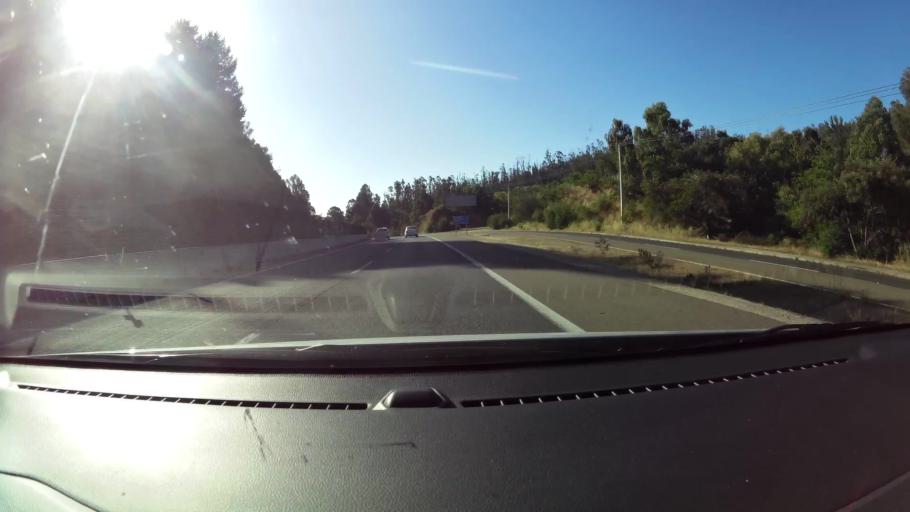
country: CL
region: Valparaiso
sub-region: Provincia de Valparaiso
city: Vina del Mar
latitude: -33.0693
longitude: -71.5761
